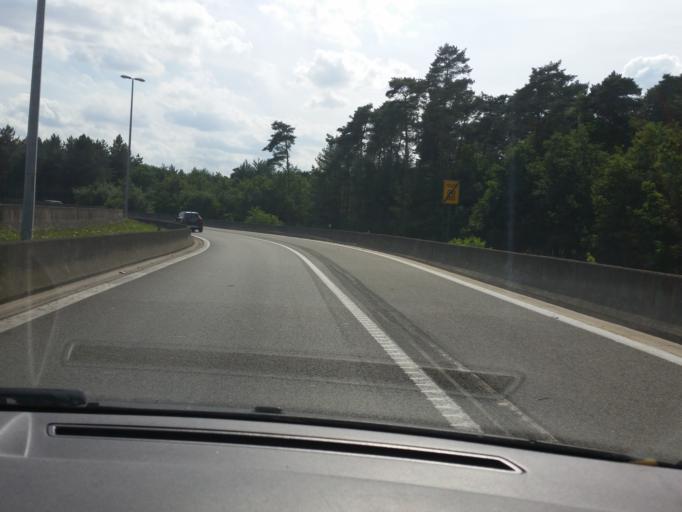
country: BE
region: Flanders
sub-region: Provincie Antwerpen
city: Brasschaat
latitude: 51.3096
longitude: 4.5532
